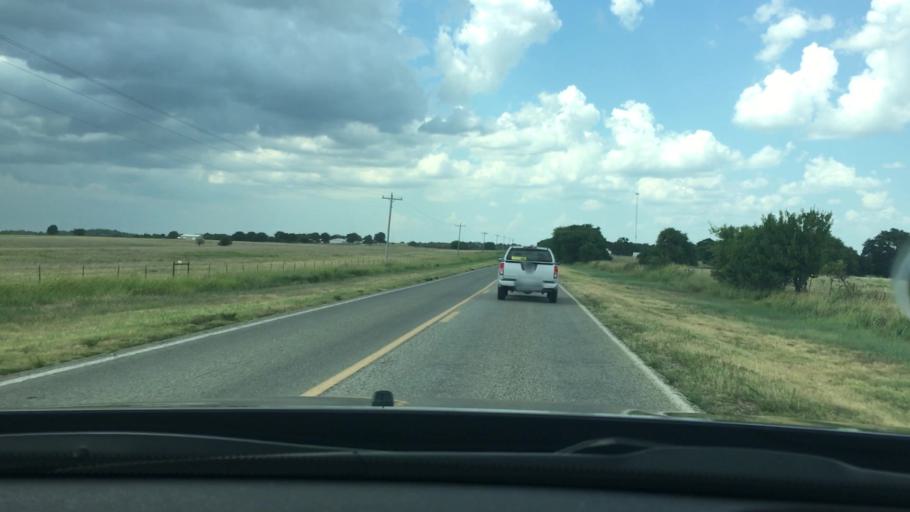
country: US
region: Oklahoma
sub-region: Pontotoc County
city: Ada
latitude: 34.5542
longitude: -96.6347
